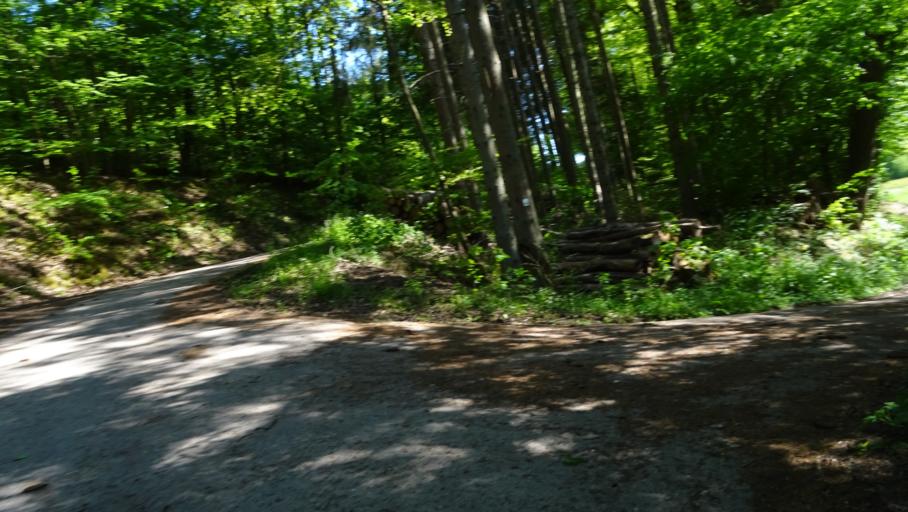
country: DE
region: Baden-Wuerttemberg
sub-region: Karlsruhe Region
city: Limbach
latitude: 49.4071
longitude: 9.2080
